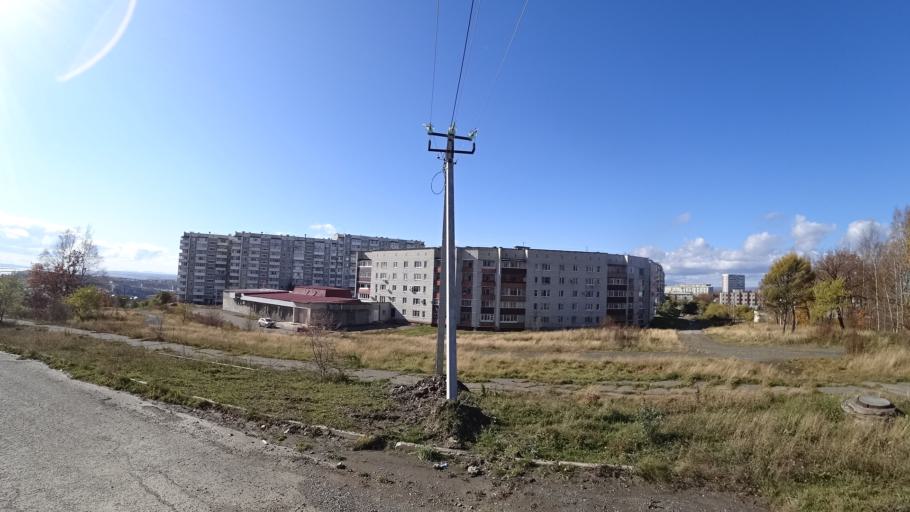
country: RU
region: Khabarovsk Krai
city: Amursk
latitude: 50.2413
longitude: 136.9197
